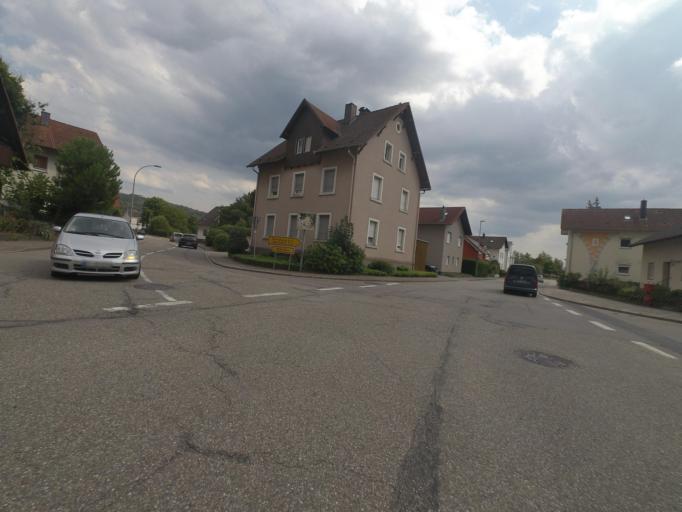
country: DE
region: Baden-Wuerttemberg
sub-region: Karlsruhe Region
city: Sinzheim
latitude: 48.7581
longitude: 8.1660
